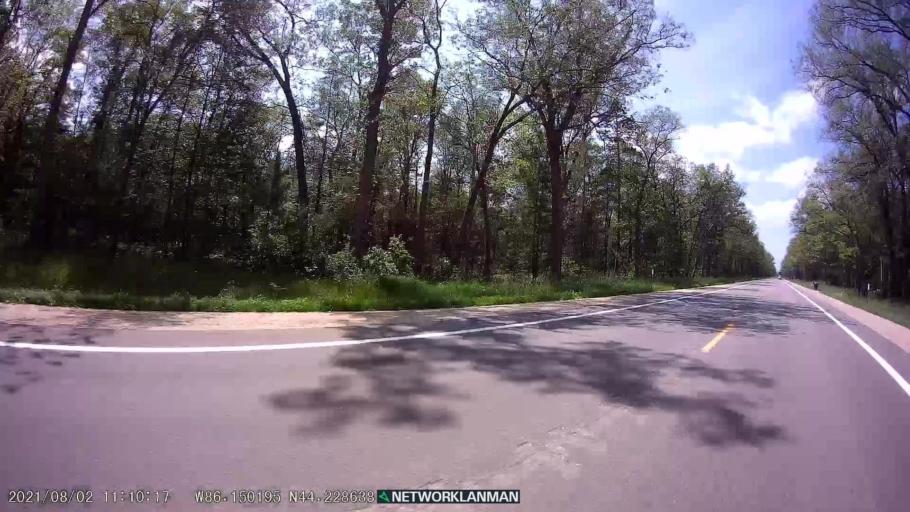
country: US
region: Michigan
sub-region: Manistee County
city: Manistee
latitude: 44.2287
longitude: -86.1508
